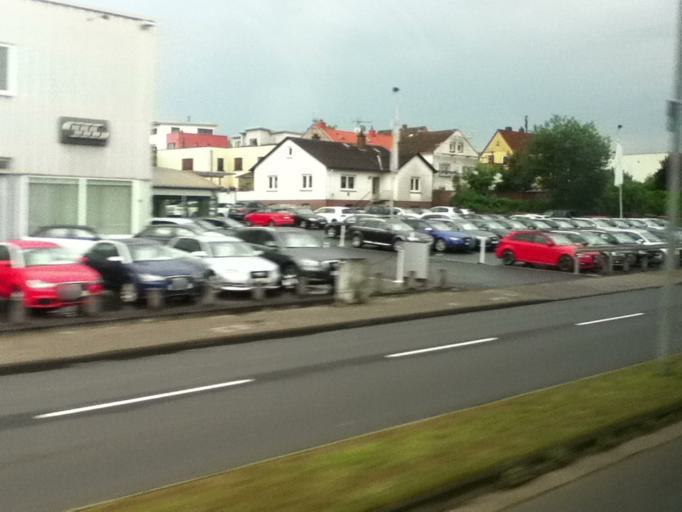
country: DE
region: Hesse
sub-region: Regierungsbezirk Giessen
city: Heuchelheim
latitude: 50.5693
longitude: 8.6554
